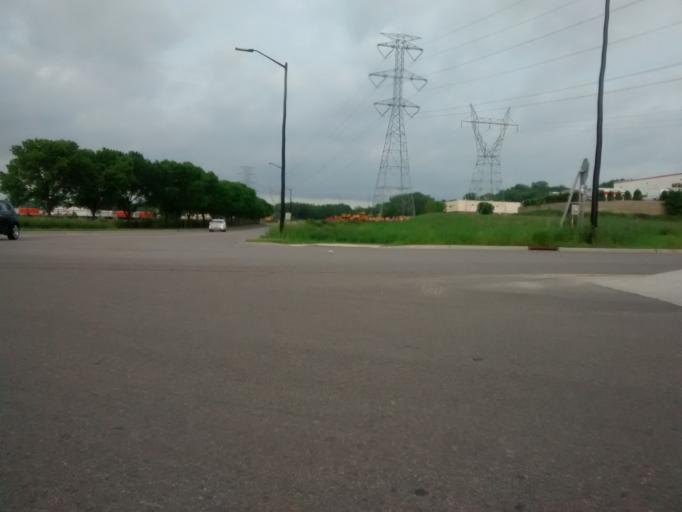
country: US
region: Minnesota
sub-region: Dakota County
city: Burnsville
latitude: 44.7757
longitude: -93.3049
